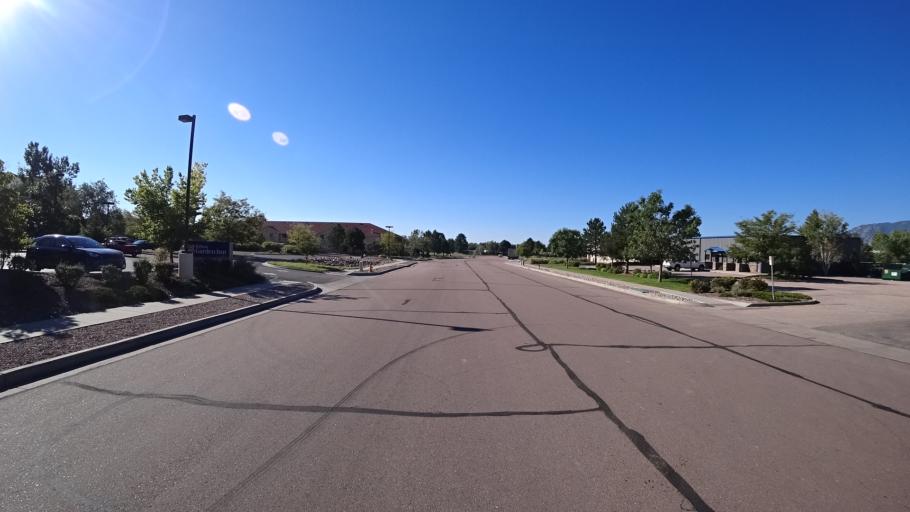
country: US
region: Colorado
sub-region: El Paso County
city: Stratmoor
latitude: 38.8010
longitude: -104.7326
